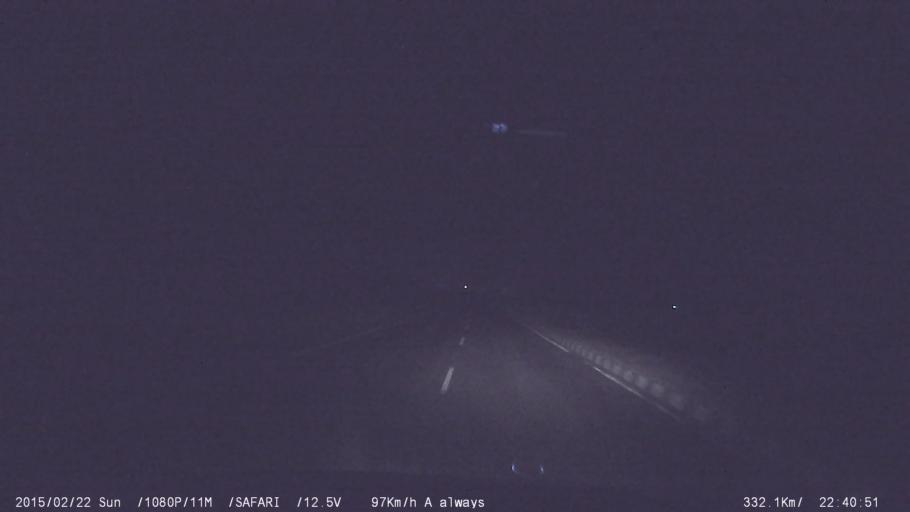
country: IN
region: Tamil Nadu
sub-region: Namakkal
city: Velur
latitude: 11.1796
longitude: 78.0636
